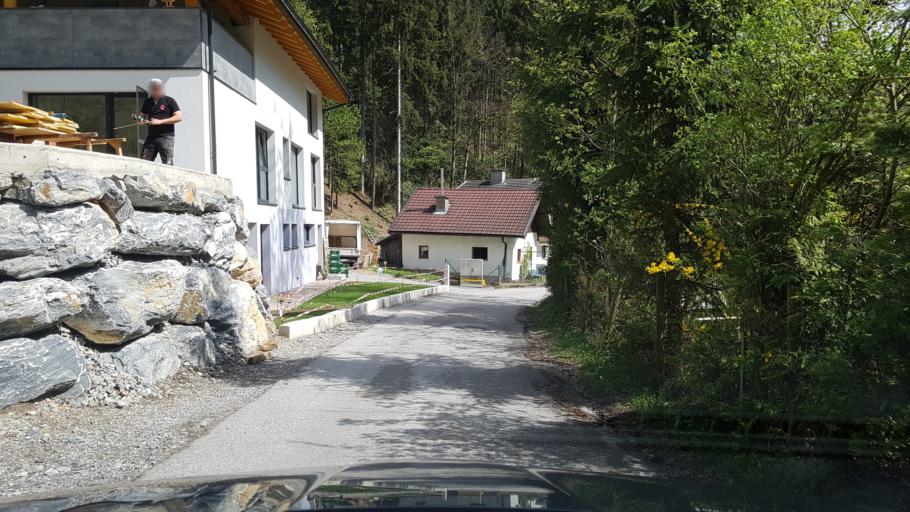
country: AT
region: Salzburg
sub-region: Politischer Bezirk Sankt Johann im Pongau
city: Werfen
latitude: 47.4630
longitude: 13.1943
